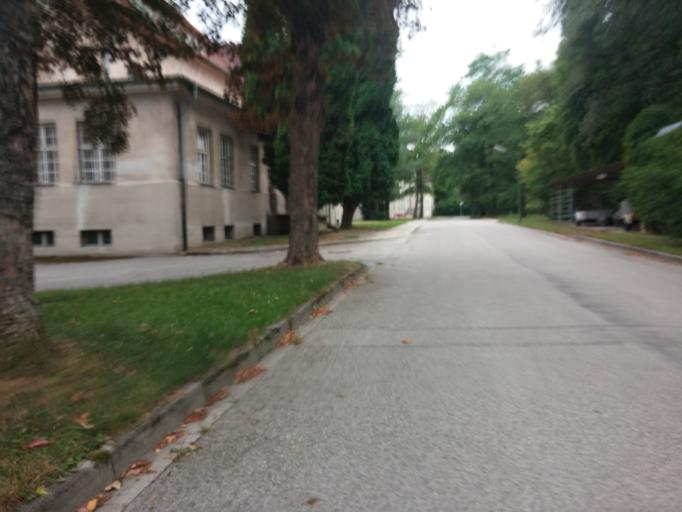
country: DE
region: Bavaria
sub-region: Upper Bavaria
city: Haar
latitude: 48.1128
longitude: 11.7418
